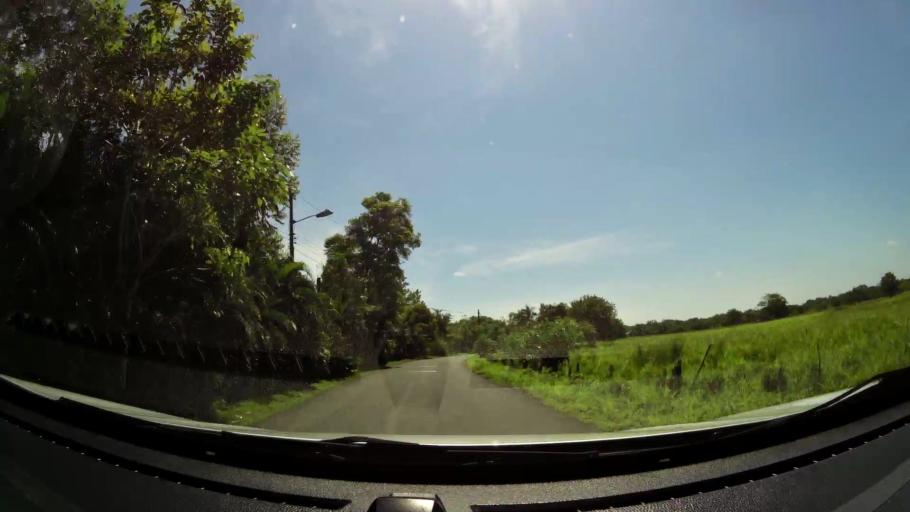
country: CR
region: Puntarenas
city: Quepos
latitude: 9.3279
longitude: -83.9575
